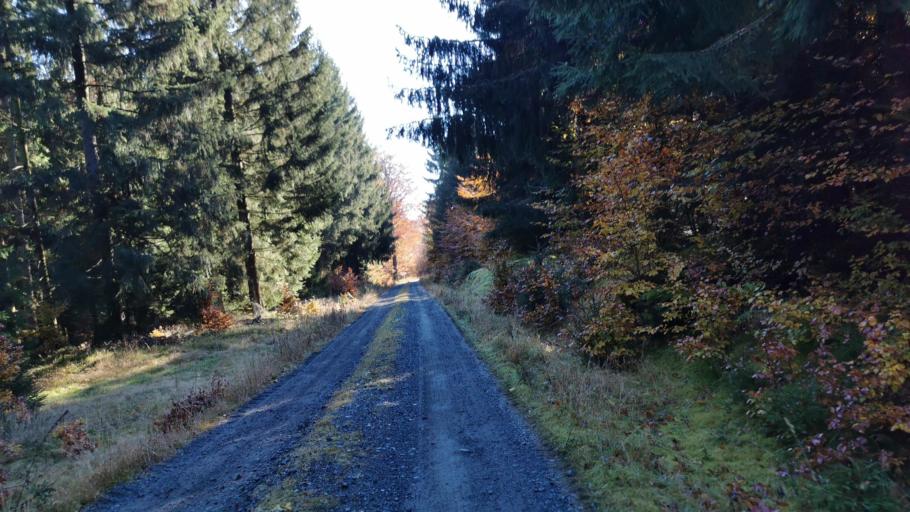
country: DE
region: Thuringia
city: Wurzbach
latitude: 50.4244
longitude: 11.5233
